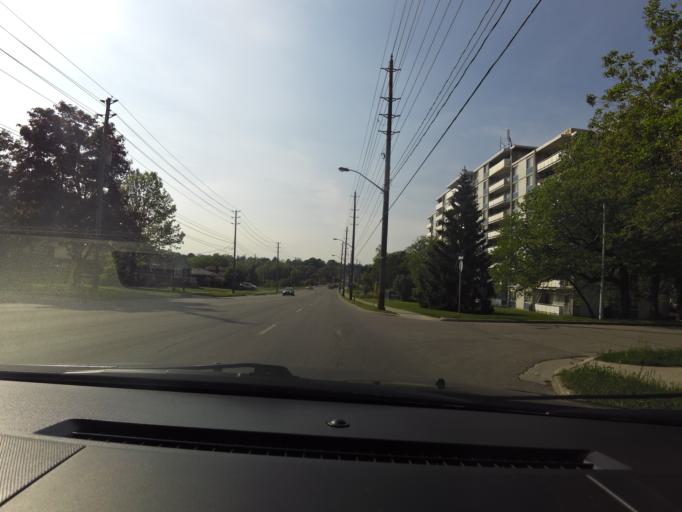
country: CA
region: Ontario
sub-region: Wellington County
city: Guelph
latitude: 43.5323
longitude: -80.2512
